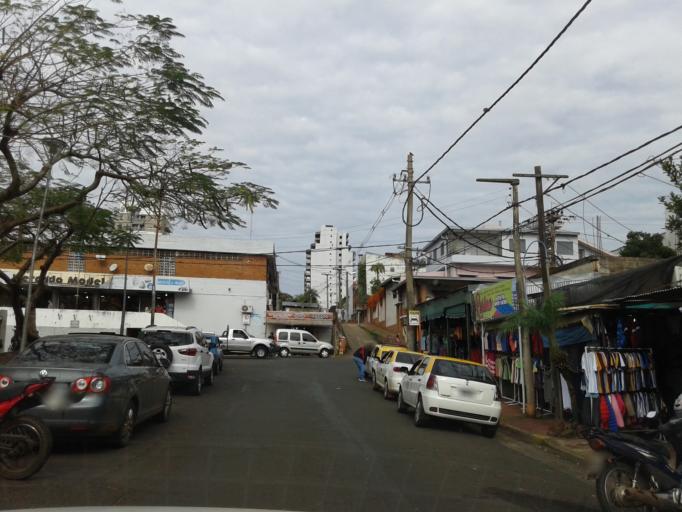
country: AR
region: Misiones
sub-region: Departamento de Capital
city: Posadas
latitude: -27.3655
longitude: -55.8870
